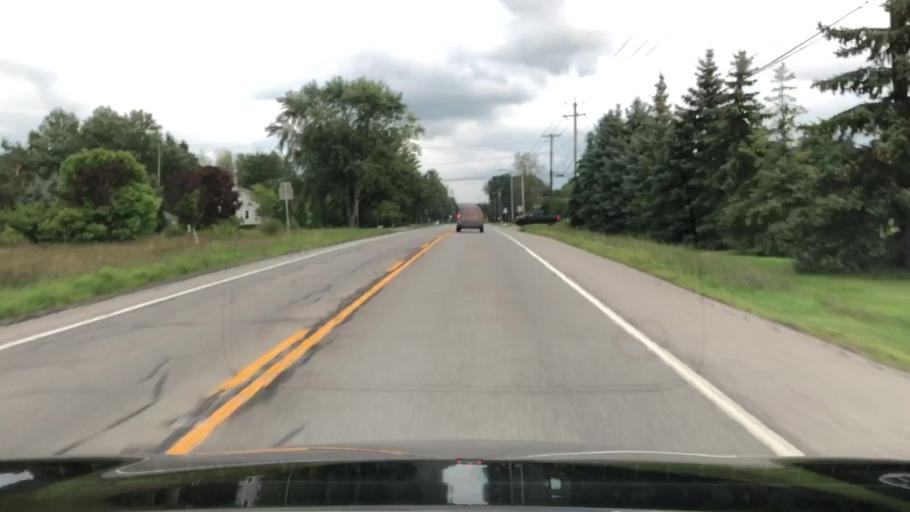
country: US
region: New York
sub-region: Erie County
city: Orchard Park
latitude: 42.7904
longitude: -78.6969
